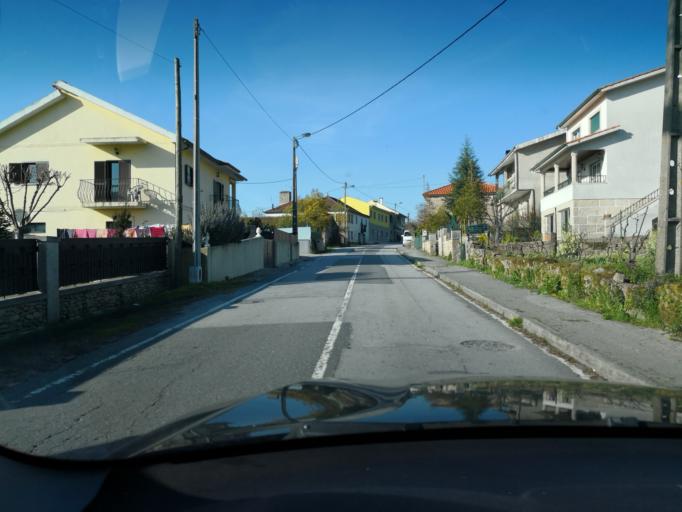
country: PT
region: Vila Real
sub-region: Vila Real
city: Vila Real
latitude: 41.3191
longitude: -7.6993
